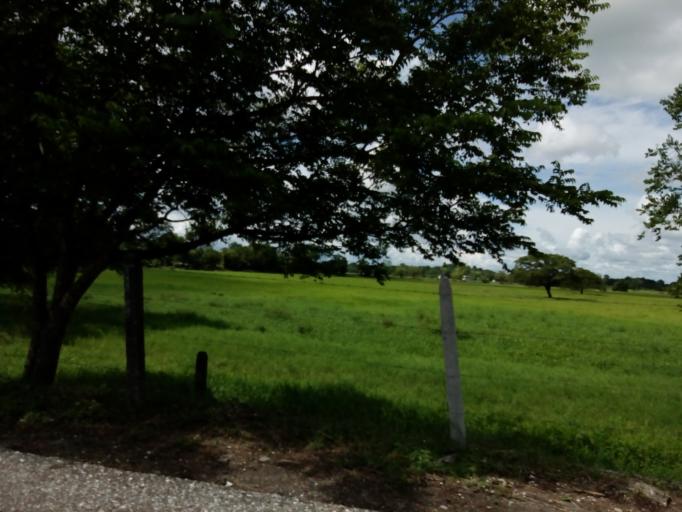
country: CO
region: Boyaca
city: Puerto Boyaca
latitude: 5.9395
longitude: -74.5682
